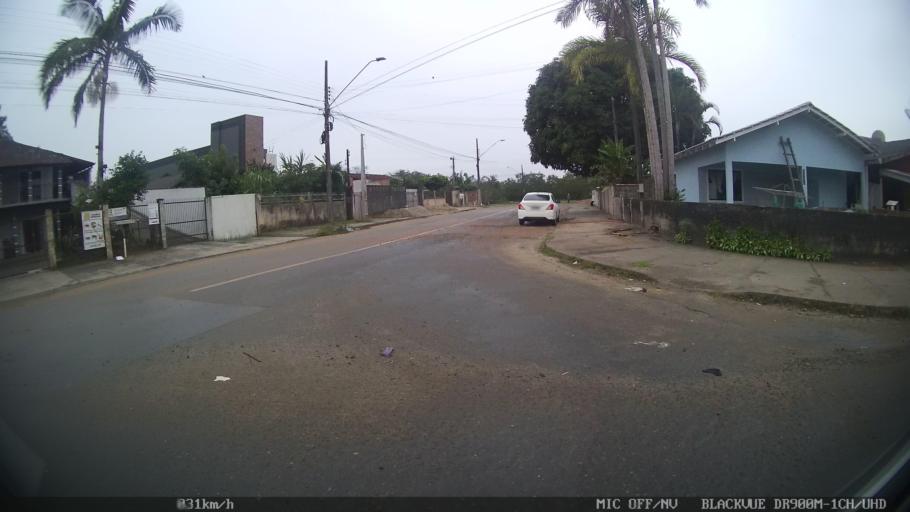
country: BR
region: Santa Catarina
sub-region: Joinville
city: Joinville
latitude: -26.2695
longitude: -48.7973
